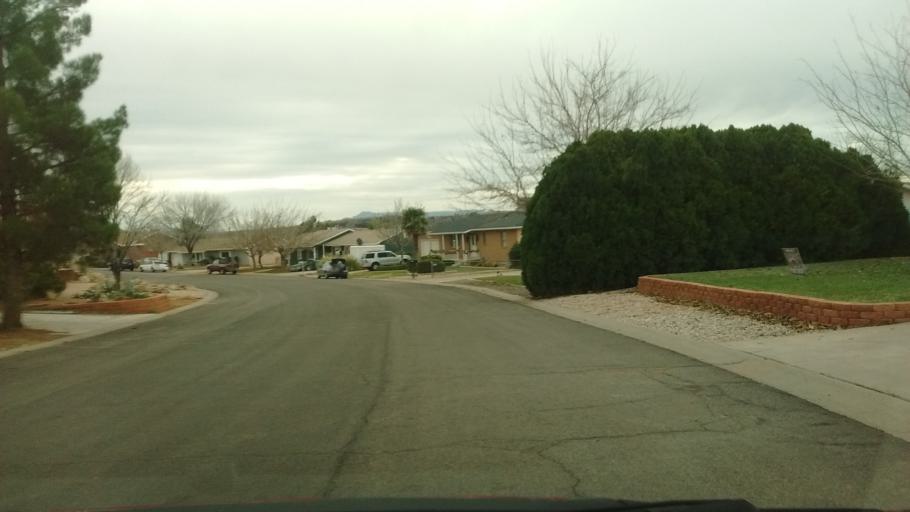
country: US
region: Utah
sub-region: Washington County
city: Washington
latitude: 37.1354
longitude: -113.4983
